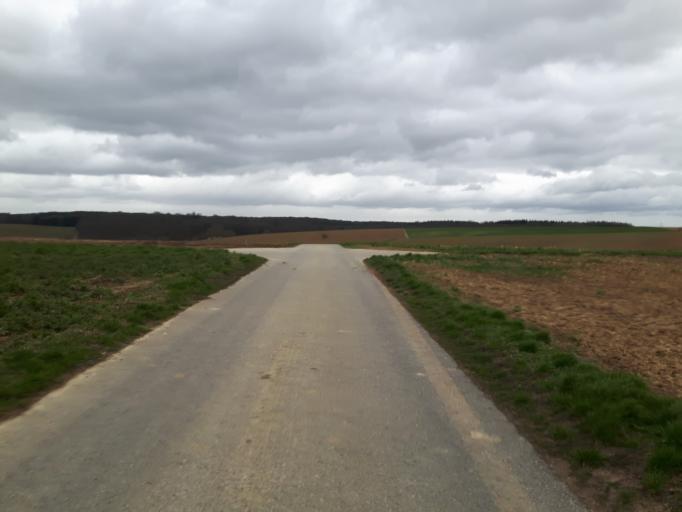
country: DE
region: Baden-Wuerttemberg
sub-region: Regierungsbezirk Stuttgart
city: Massenbachhausen
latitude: 49.1758
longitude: 9.0749
